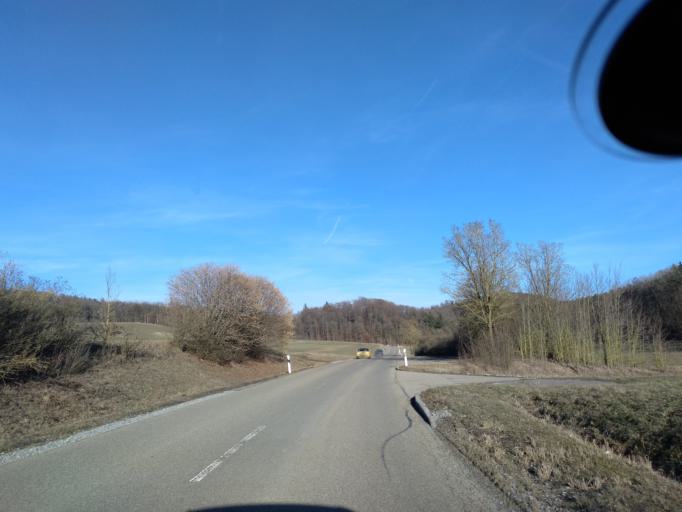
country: DE
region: Baden-Wuerttemberg
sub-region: Regierungsbezirk Stuttgart
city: Obersontheim
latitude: 49.0868
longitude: 9.9159
